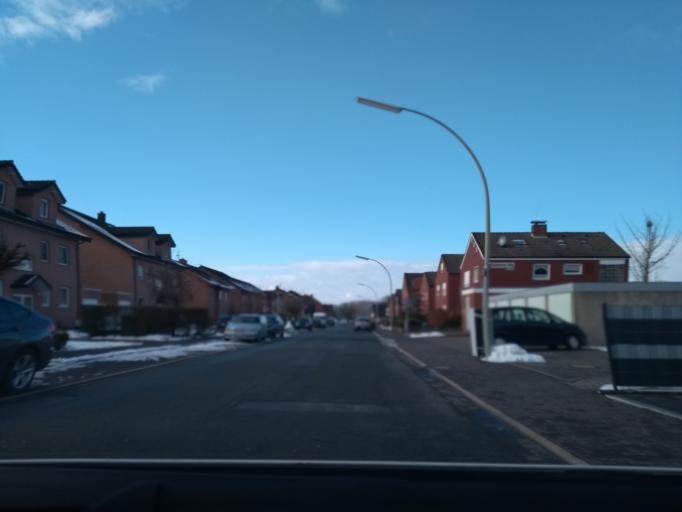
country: DE
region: North Rhine-Westphalia
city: Selm
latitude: 51.6947
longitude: 7.4514
